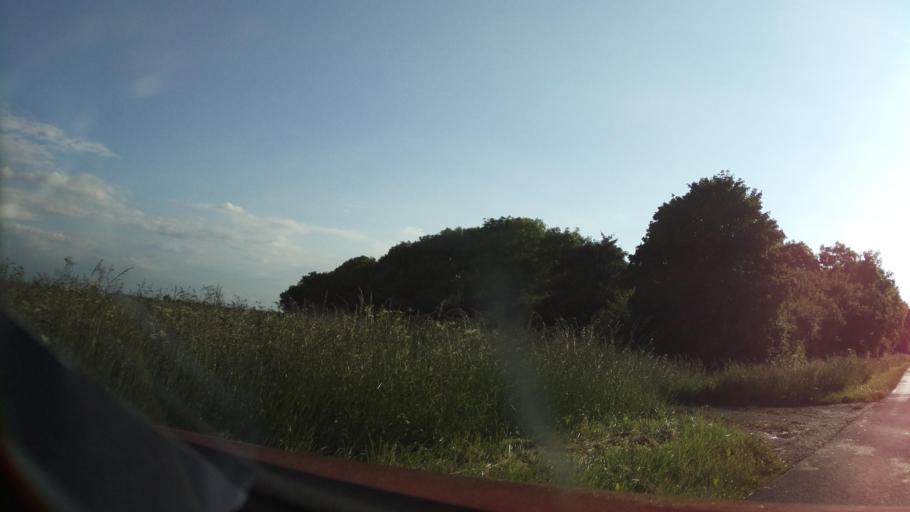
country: GB
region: England
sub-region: Lincolnshire
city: Navenby
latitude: 53.1135
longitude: -0.6016
